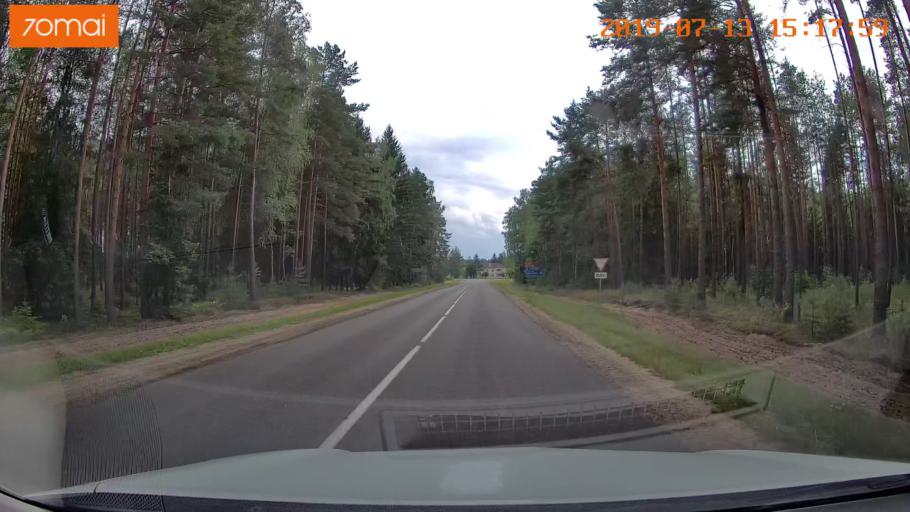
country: BY
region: Mogilev
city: Hlusha
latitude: 53.0890
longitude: 28.8461
